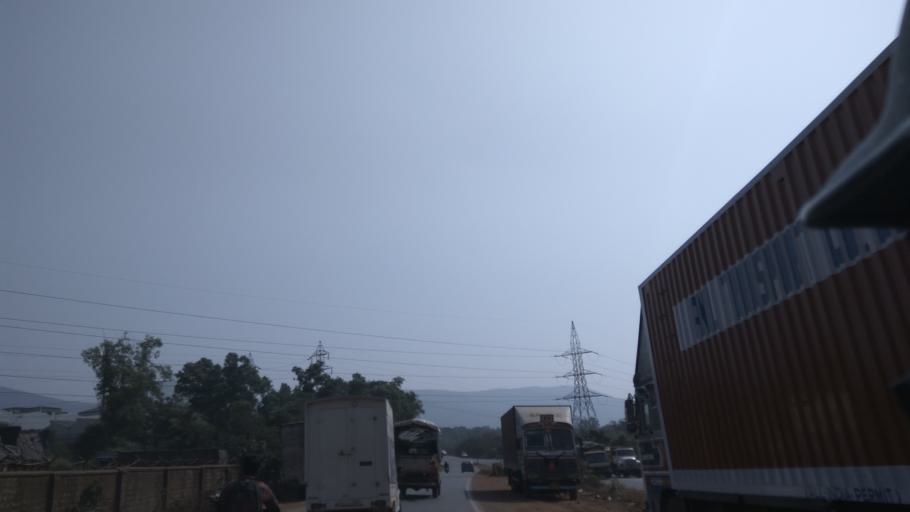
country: IN
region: Goa
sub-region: North Goa
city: Palle
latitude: 15.4165
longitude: 74.0713
